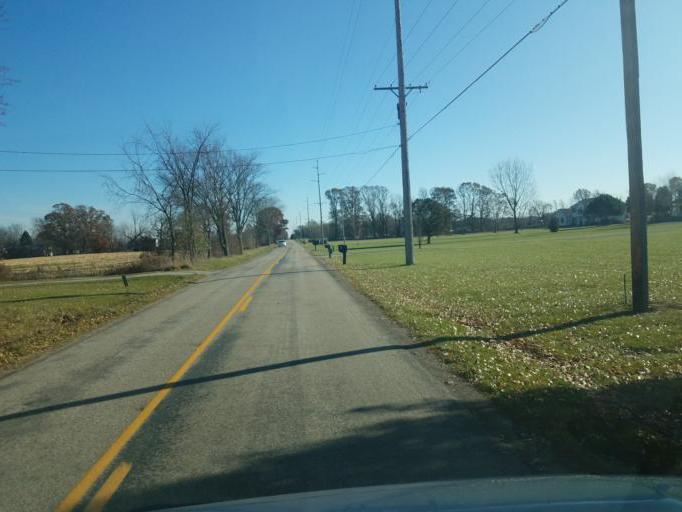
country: US
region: Ohio
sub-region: Ashland County
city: Ashland
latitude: 40.8290
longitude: -82.3425
